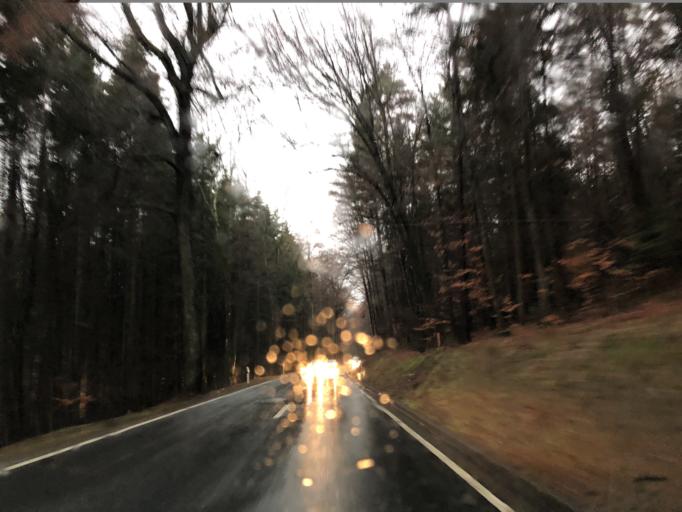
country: DE
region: Hesse
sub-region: Regierungsbezirk Darmstadt
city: Bad Konig
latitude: 49.7313
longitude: 9.0494
